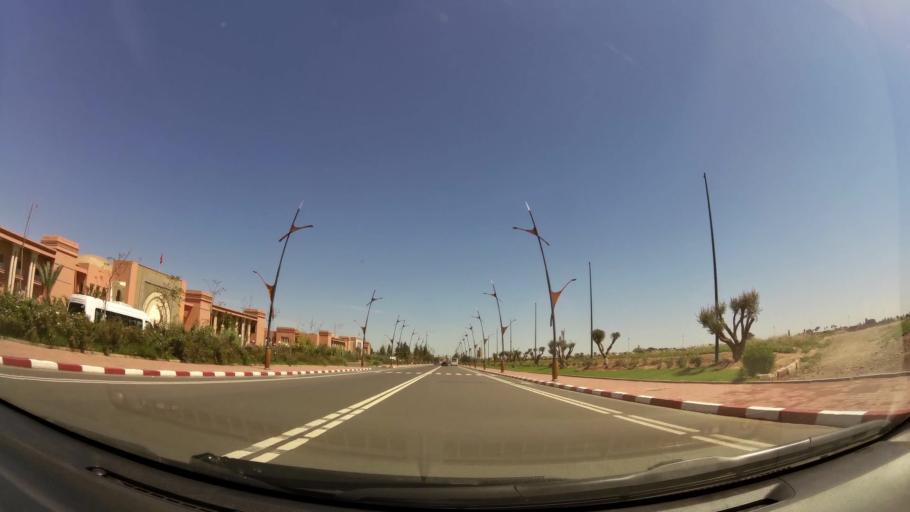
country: MA
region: Marrakech-Tensift-Al Haouz
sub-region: Marrakech
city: Marrakesh
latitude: 31.6106
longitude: -7.9950
